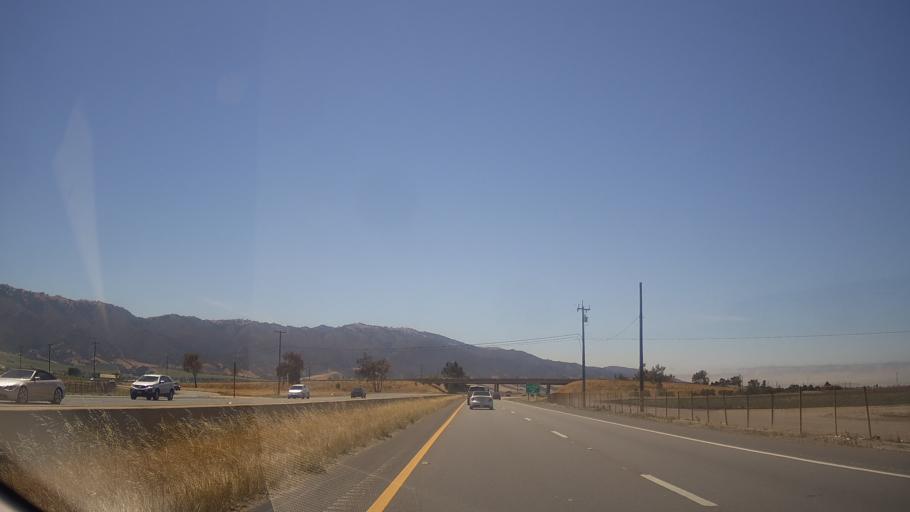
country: US
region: California
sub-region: Monterey County
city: Gonzales
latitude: 36.5219
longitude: -121.4582
